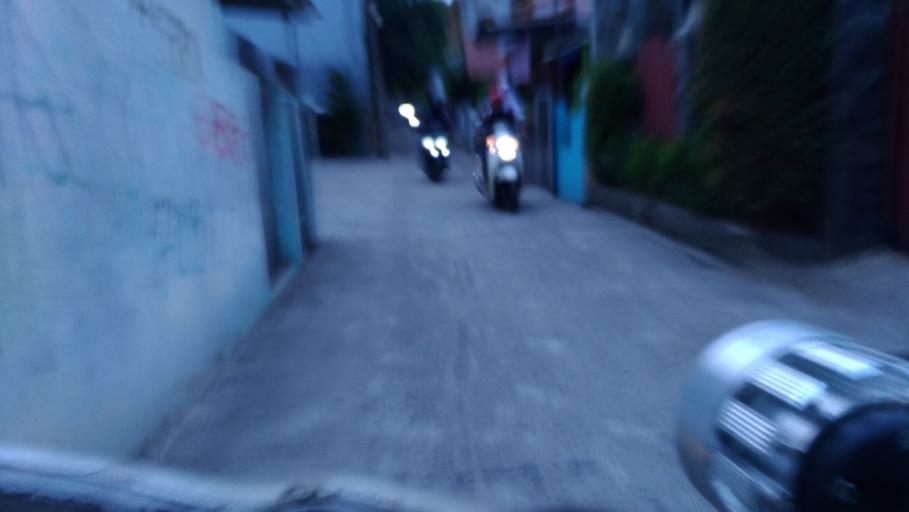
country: ID
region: West Java
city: Depok
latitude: -6.3531
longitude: 106.8772
